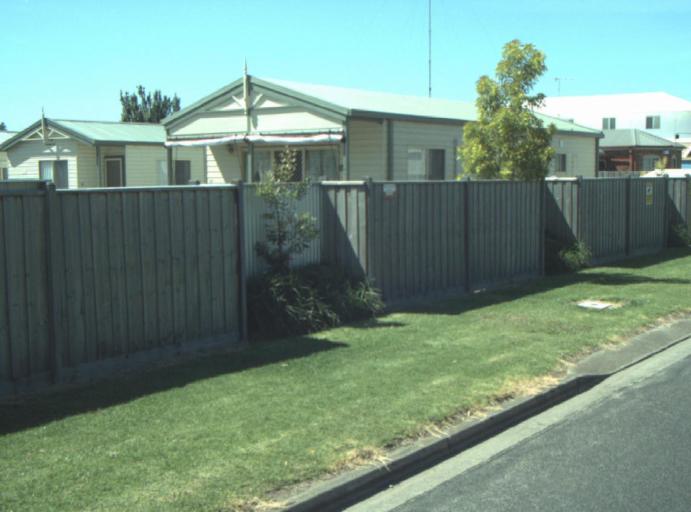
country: AU
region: Victoria
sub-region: Greater Geelong
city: Leopold
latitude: -38.2660
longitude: 144.5149
